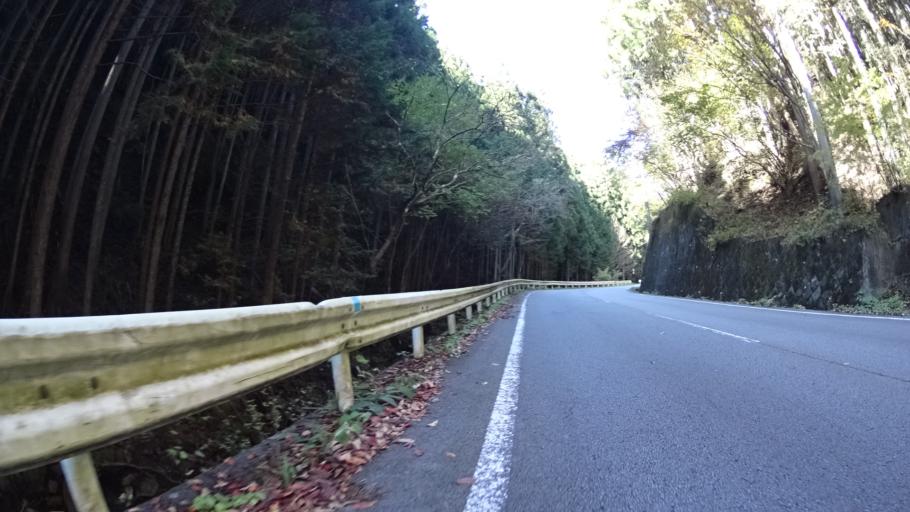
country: JP
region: Yamanashi
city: Otsuki
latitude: 35.7650
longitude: 138.9365
